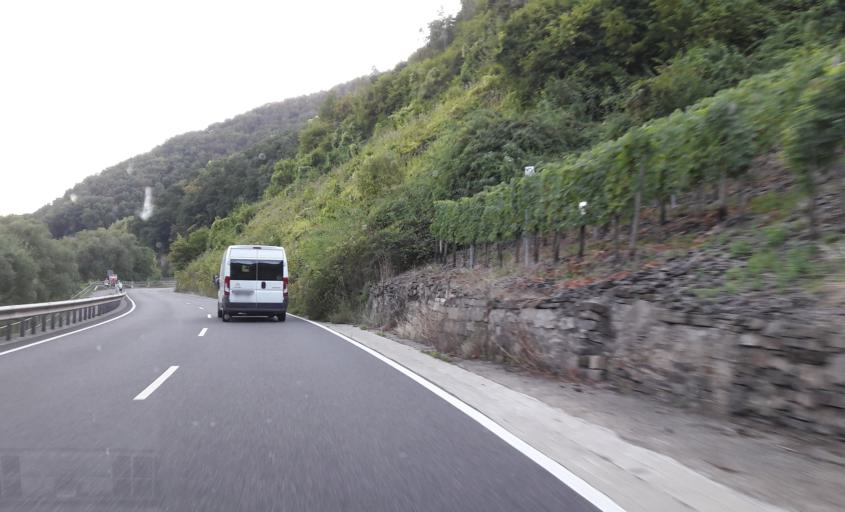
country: DE
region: Rheinland-Pfalz
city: Bruttig-Fankel
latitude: 50.1268
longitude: 7.2245
